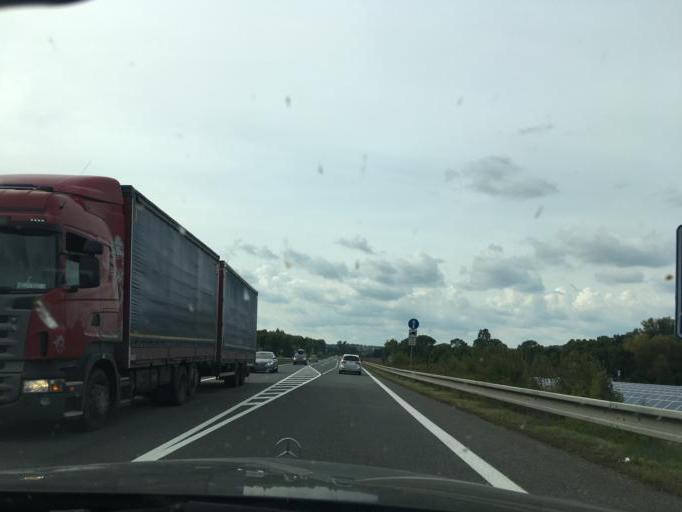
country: CZ
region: Kralovehradecky
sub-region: Okres Nachod
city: Ceska Skalice
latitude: 50.3864
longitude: 16.0295
